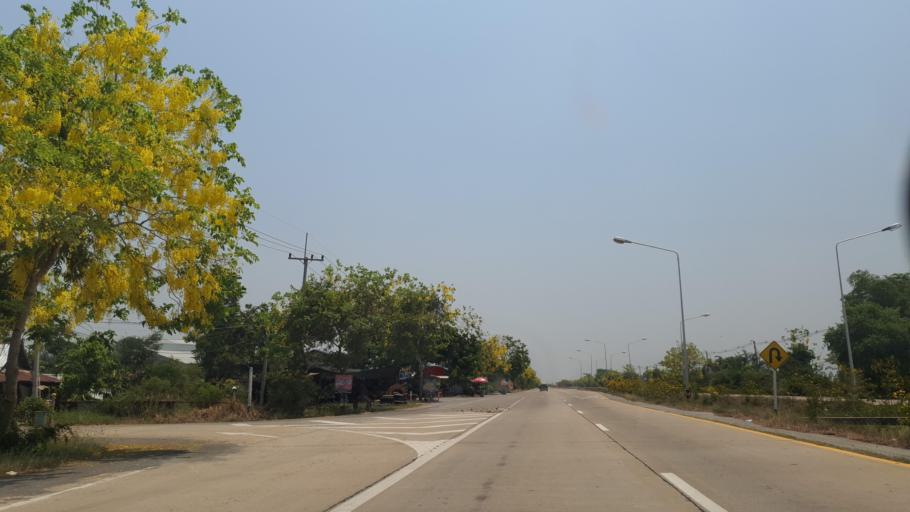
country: TH
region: Suphan Buri
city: Suphan Buri
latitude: 14.5424
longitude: 100.0721
